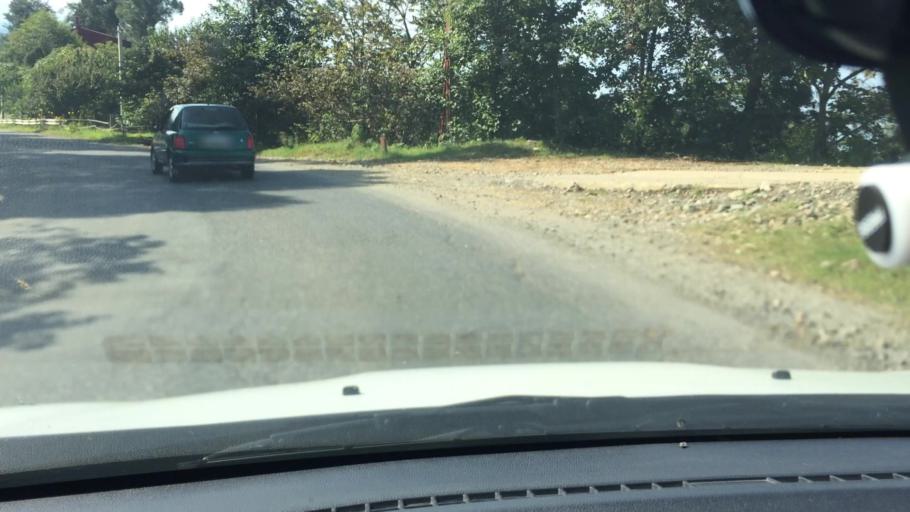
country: GE
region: Ajaria
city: Kobuleti
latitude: 41.7500
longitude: 41.7426
